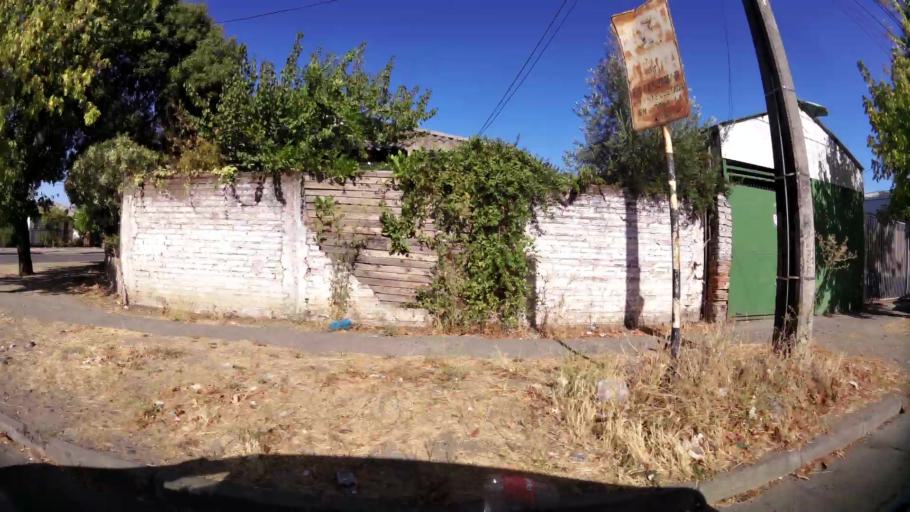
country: CL
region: Maule
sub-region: Provincia de Talca
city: Talca
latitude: -35.4164
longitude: -71.6503
